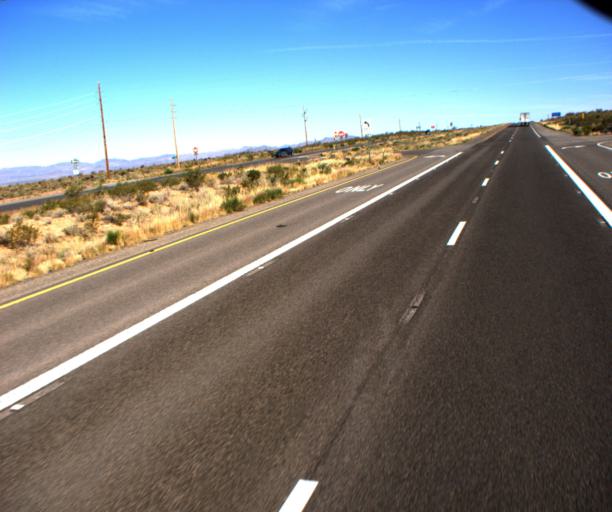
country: US
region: Arizona
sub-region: Mohave County
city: Golden Valley
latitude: 35.2431
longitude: -114.1477
